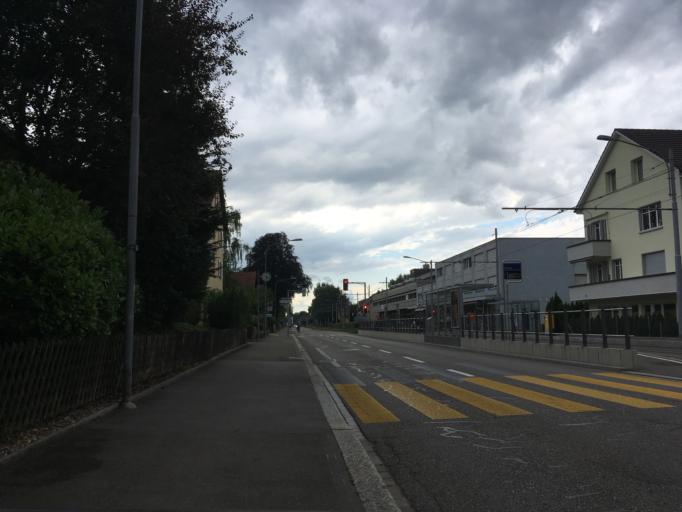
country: CH
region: Zurich
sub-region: Bezirk Zuerich
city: Zuerich (Kreis 12) / Hirzenbach
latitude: 47.4001
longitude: 8.5868
